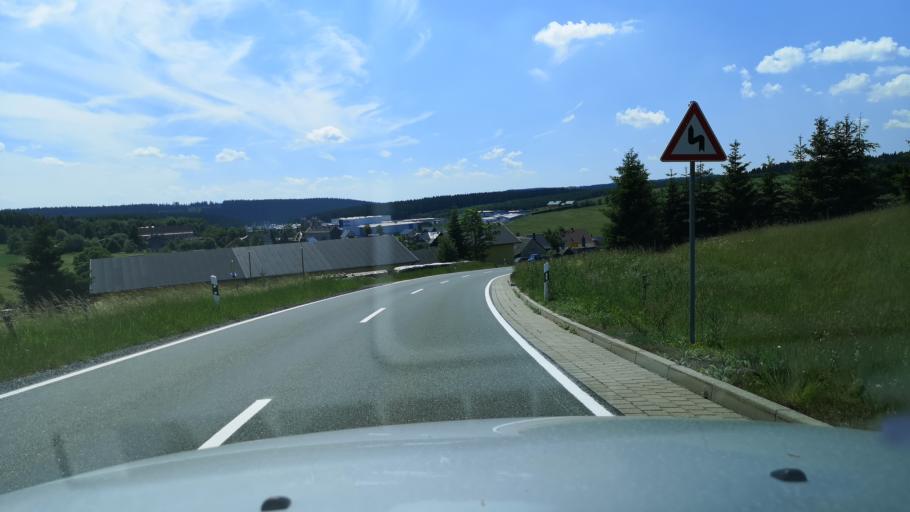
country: DE
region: Bavaria
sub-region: Upper Franconia
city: Tettau
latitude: 50.4973
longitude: 11.2567
